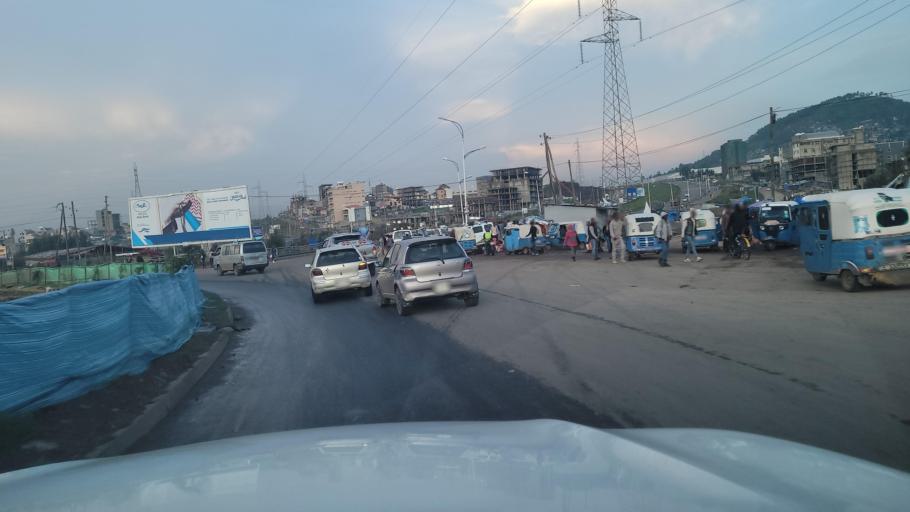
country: ET
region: Adis Abeba
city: Addis Ababa
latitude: 8.9540
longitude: 38.6968
